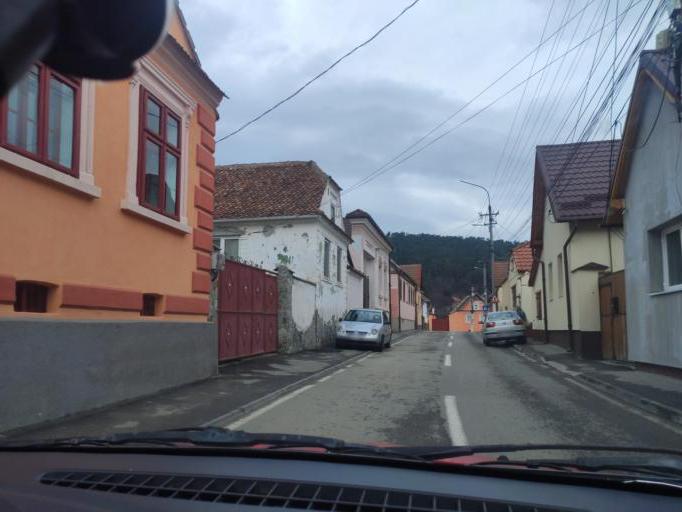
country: RO
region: Brasov
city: Codlea
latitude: 45.6978
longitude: 25.4393
